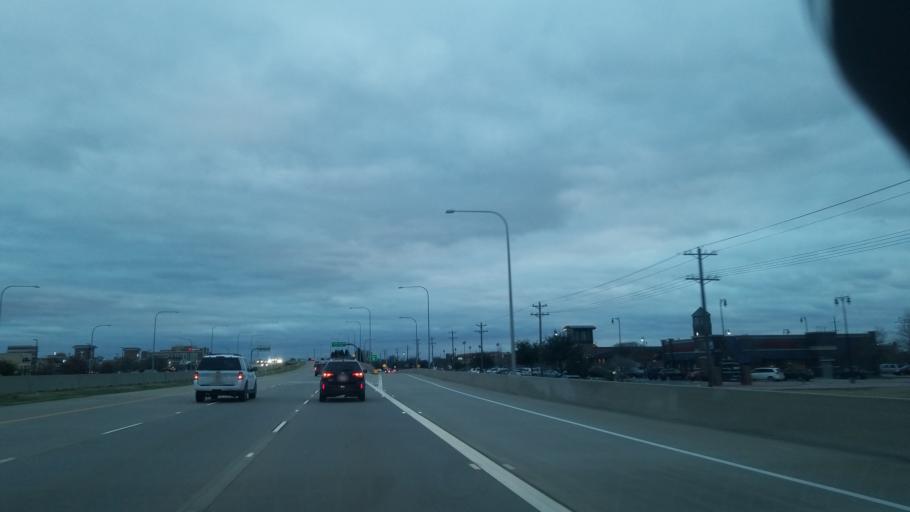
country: US
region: Texas
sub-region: Collin County
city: Frisco
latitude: 33.1578
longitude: -96.8403
